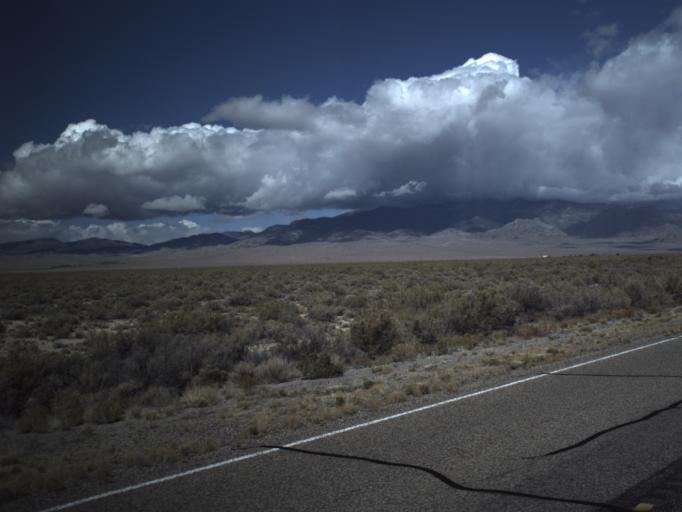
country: US
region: Nevada
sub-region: White Pine County
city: McGill
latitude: 39.0315
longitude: -114.0358
